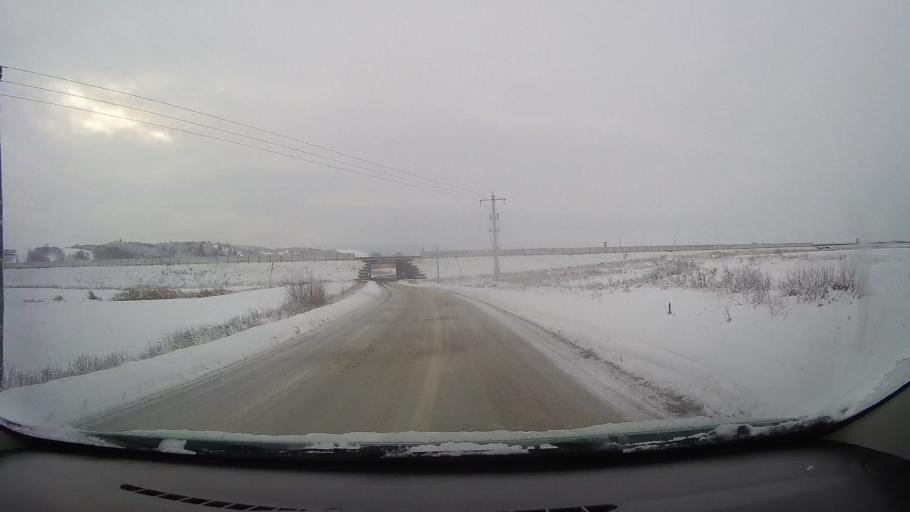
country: RO
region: Alba
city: Vurpar
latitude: 45.9689
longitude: 23.4794
